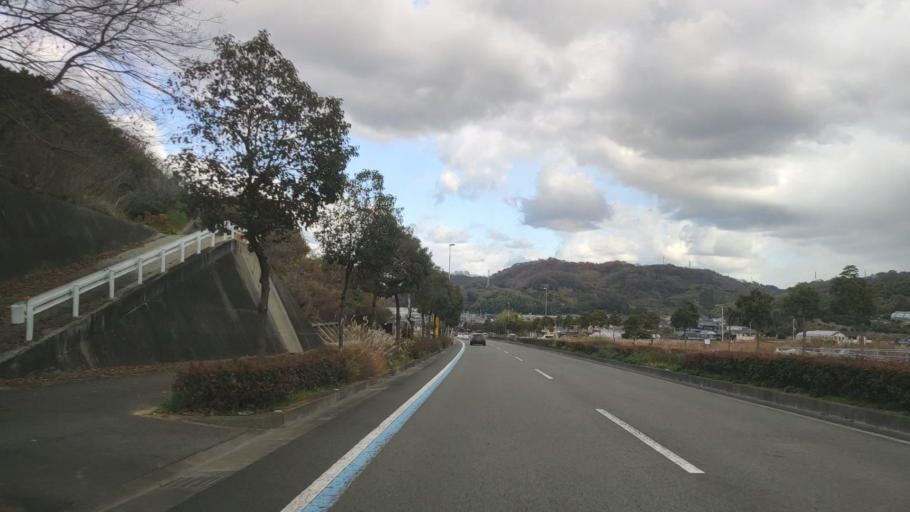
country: JP
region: Ehime
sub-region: Shikoku-chuo Shi
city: Matsuyama
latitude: 33.8933
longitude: 132.7578
